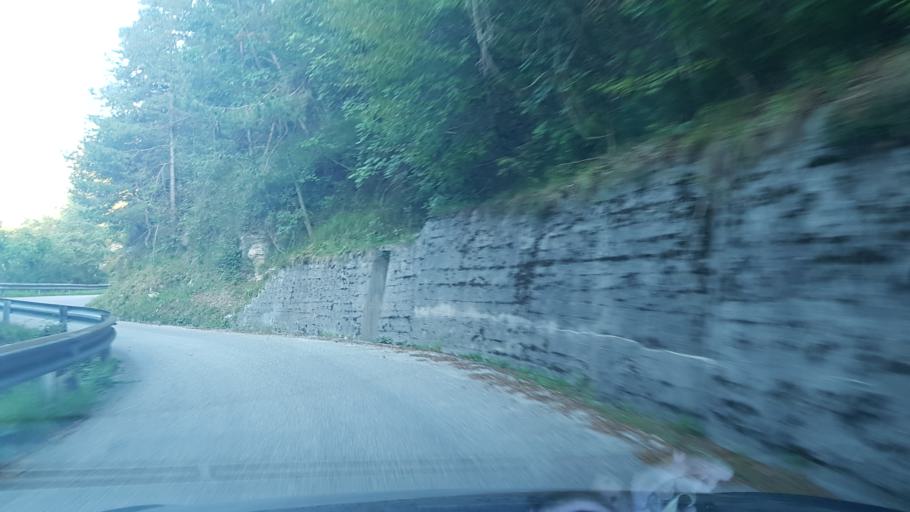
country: IT
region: Friuli Venezia Giulia
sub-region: Provincia di Pordenone
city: Frisanco
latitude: 46.2561
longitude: 12.7313
